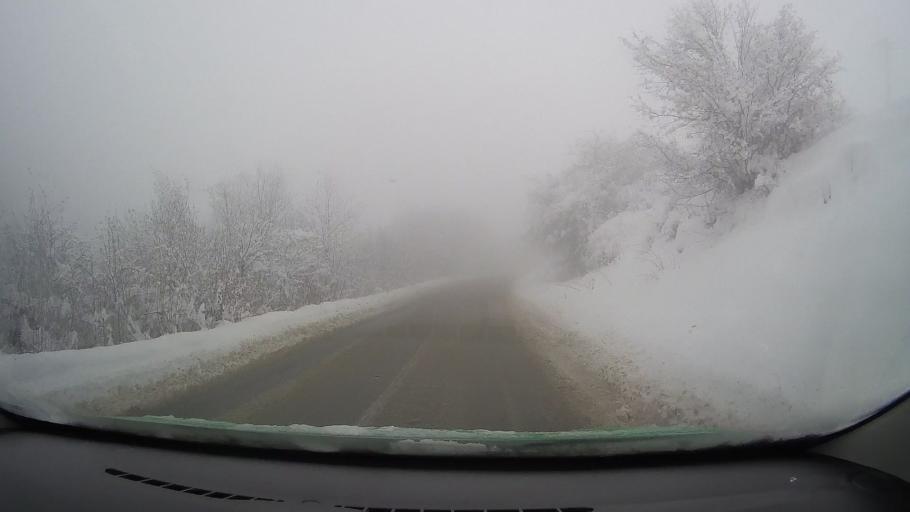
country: RO
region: Sibiu
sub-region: Comuna Poiana Sibiului
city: Poiana Sibiului
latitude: 45.8071
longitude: 23.7471
